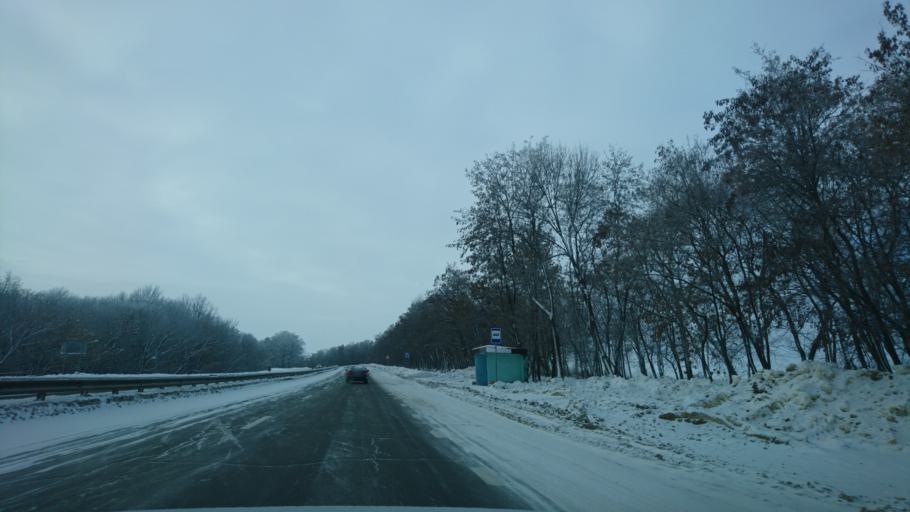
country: RU
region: Belgorod
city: Mayskiy
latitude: 50.4854
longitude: 36.4106
